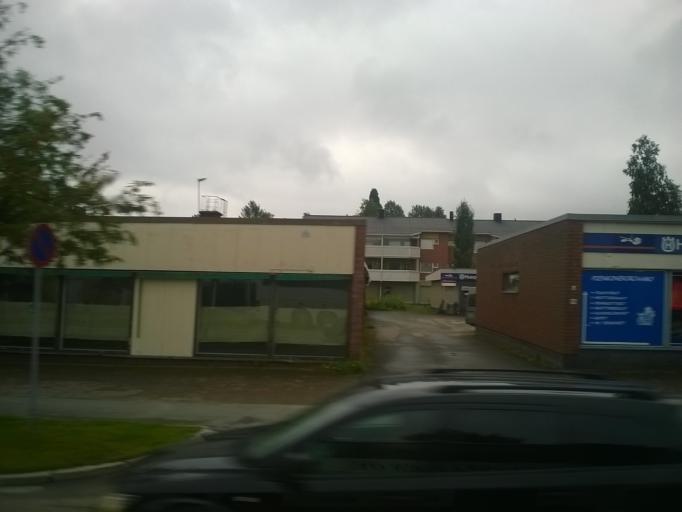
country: FI
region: Kainuu
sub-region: Kehys-Kainuu
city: Kuhmo
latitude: 64.1270
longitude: 29.5169
